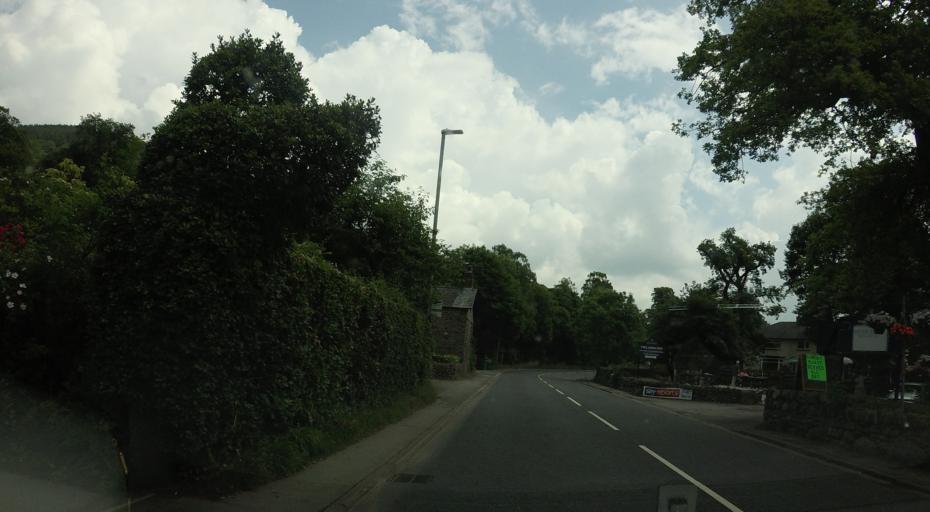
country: GB
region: England
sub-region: Cumbria
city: Keswick
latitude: 54.6046
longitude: -3.1235
